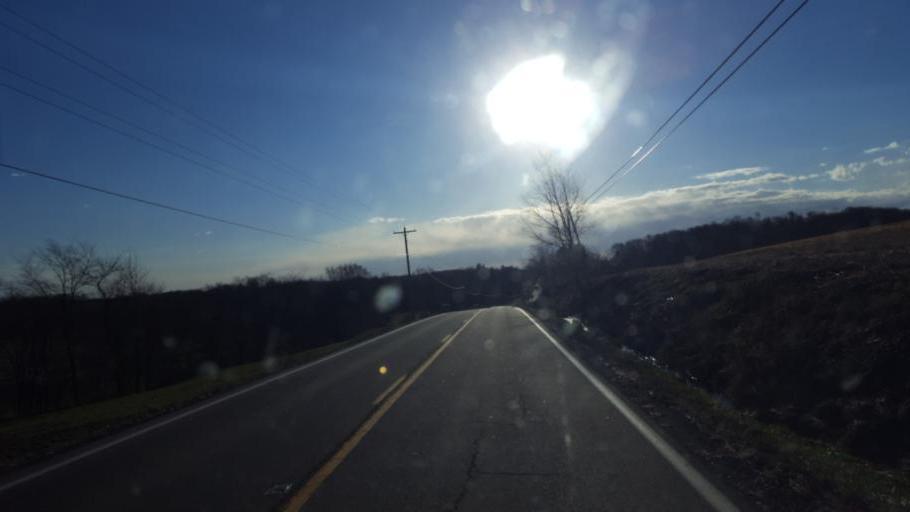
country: US
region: Ohio
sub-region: Wayne County
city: Shreve
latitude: 40.5904
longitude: -82.0797
